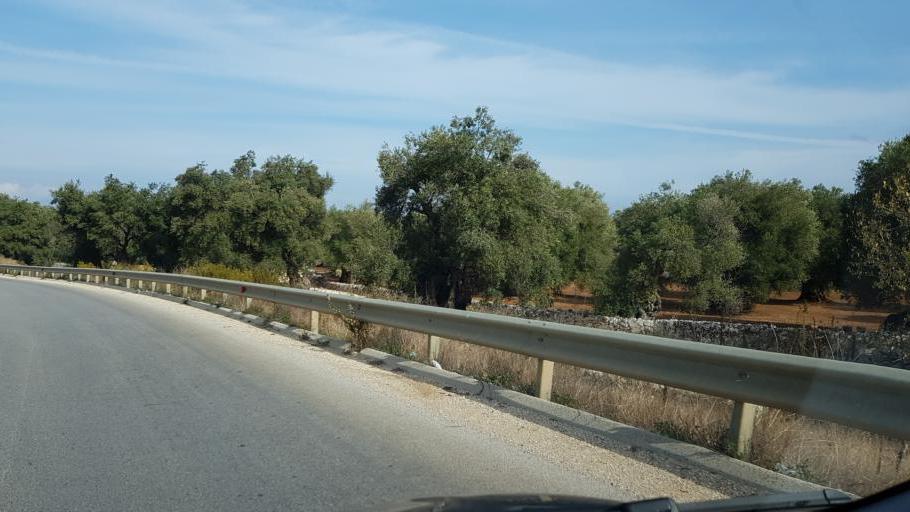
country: IT
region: Apulia
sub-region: Provincia di Brindisi
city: Ostuni
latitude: 40.7461
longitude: 17.5823
